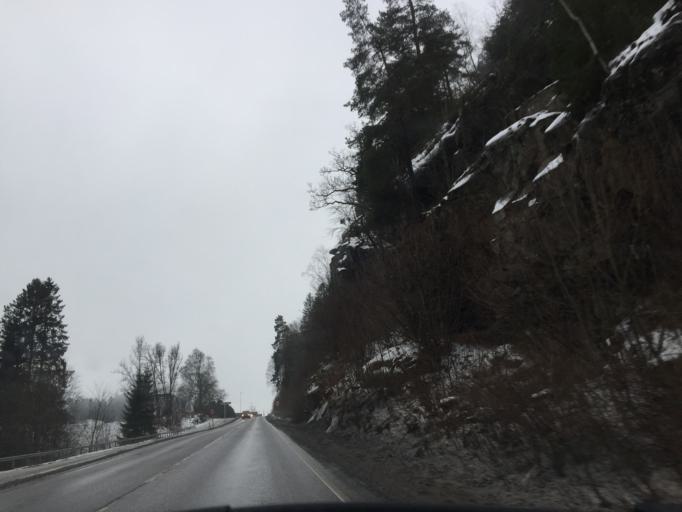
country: NO
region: Akershus
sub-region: Frogn
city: Drobak
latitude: 59.6774
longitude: 10.6612
